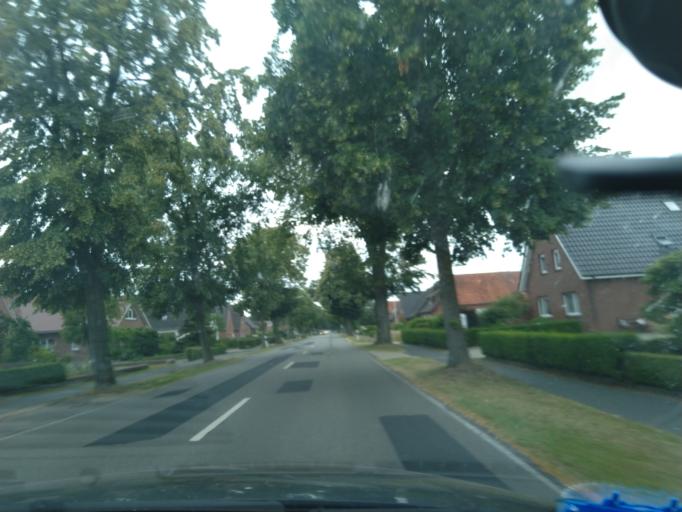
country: DE
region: Lower Saxony
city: Papenburg
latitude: 53.0613
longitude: 7.3559
